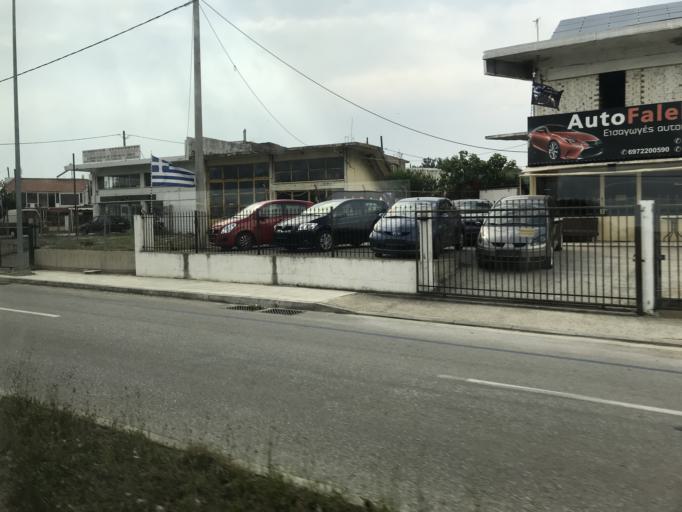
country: GR
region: East Macedonia and Thrace
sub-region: Nomos Evrou
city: Alexandroupoli
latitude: 40.8519
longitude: 25.9056
